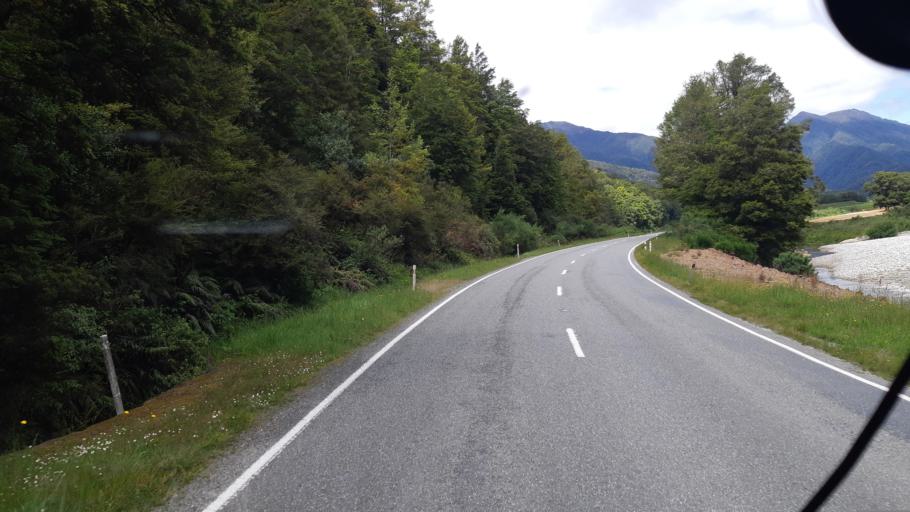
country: NZ
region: West Coast
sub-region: Buller District
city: Westport
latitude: -42.1592
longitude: 171.9218
